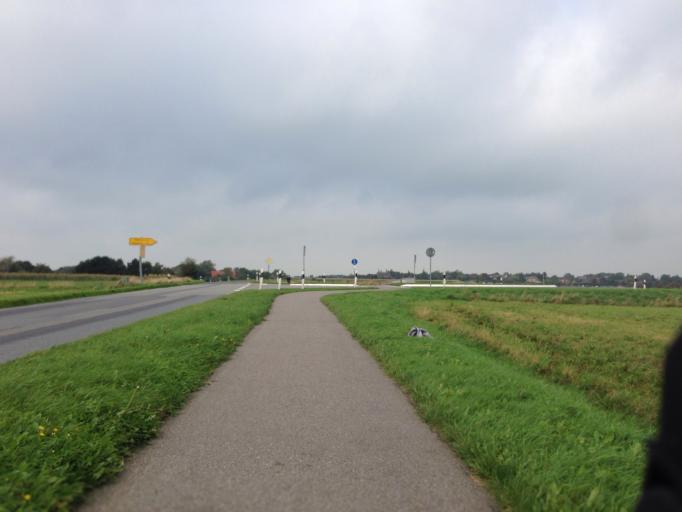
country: DE
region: Schleswig-Holstein
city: Wrixum
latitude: 54.7032
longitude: 8.5400
